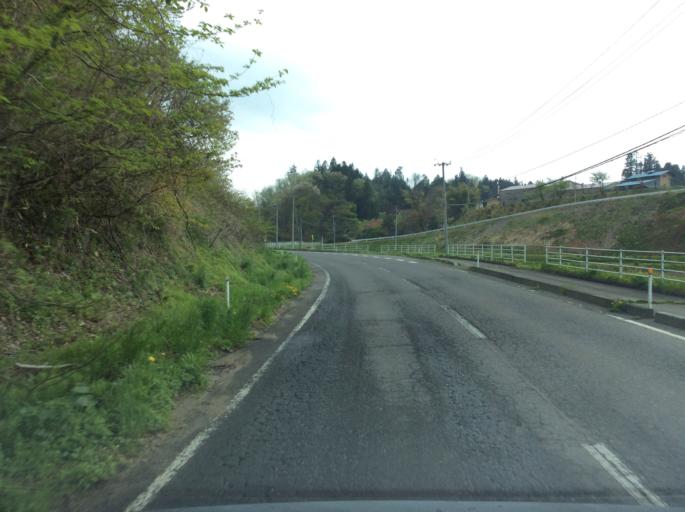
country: JP
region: Fukushima
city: Funehikimachi-funehiki
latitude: 37.4031
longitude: 140.5380
